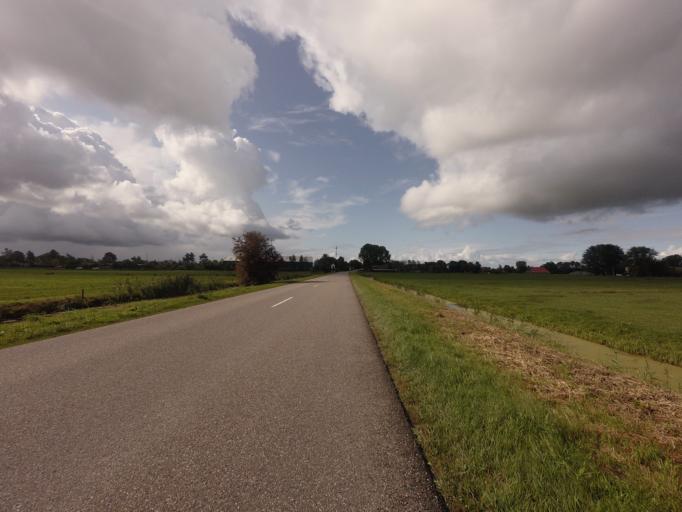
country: NL
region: Friesland
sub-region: Gemeente Boarnsterhim
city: Warten
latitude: 53.1529
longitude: 5.9079
